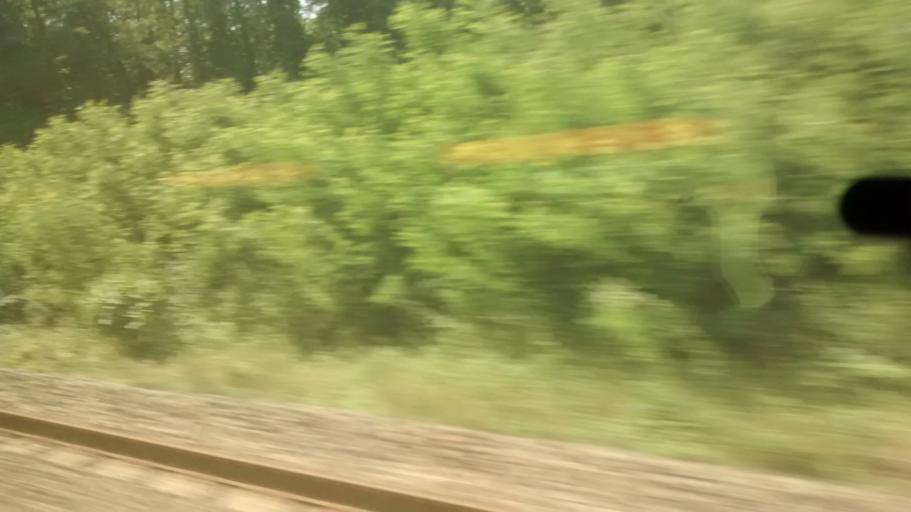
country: FR
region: Rhone-Alpes
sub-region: Departement de l'Ain
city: Grieges
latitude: 46.2428
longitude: 4.8507
